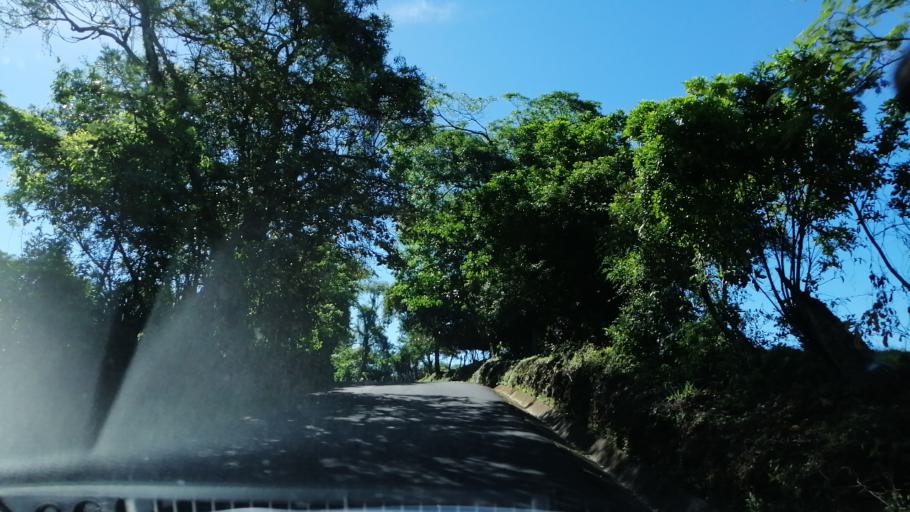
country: SV
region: Morazan
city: Corinto
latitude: 13.8117
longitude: -87.9828
